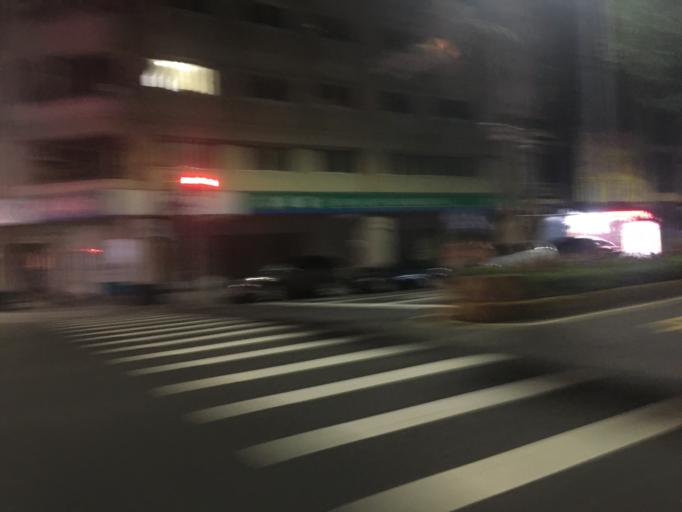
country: TW
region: Taiwan
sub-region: Hsinchu
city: Hsinchu
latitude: 24.8021
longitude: 120.9545
